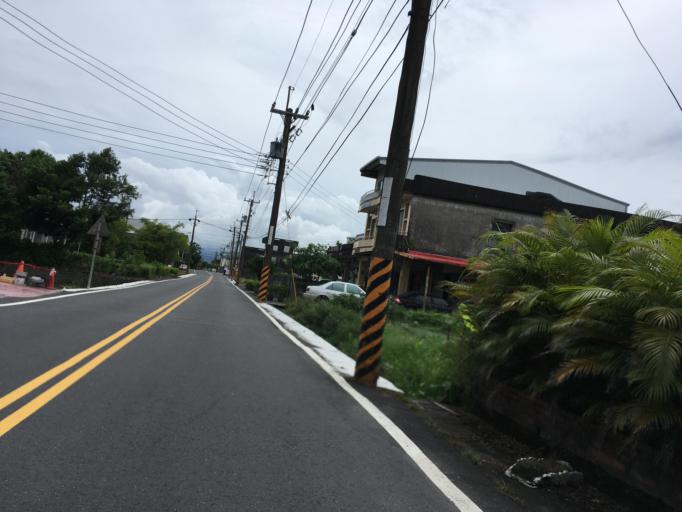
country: TW
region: Taiwan
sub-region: Yilan
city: Yilan
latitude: 24.6961
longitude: 121.8112
